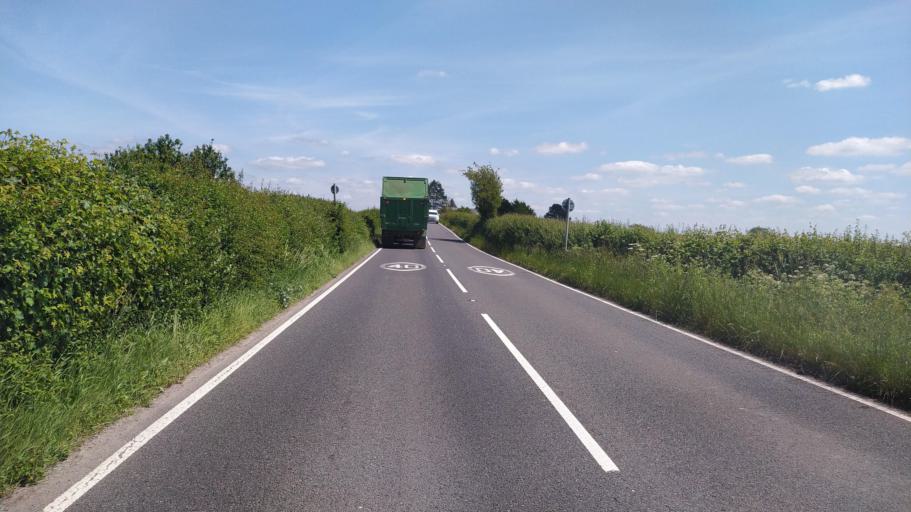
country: GB
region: England
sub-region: Somerset
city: Ilchester
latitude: 51.0299
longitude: -2.7173
